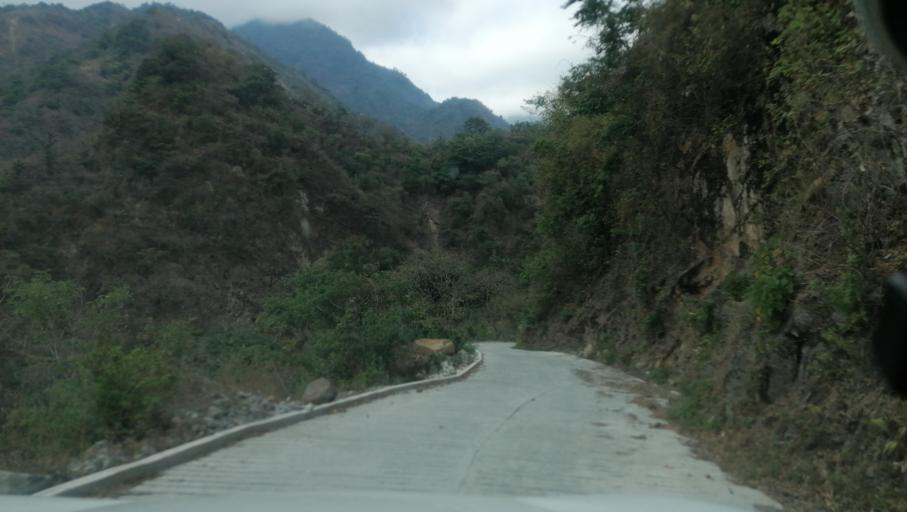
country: MX
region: Chiapas
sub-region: Cacahoatan
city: Benito Juarez
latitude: 15.1646
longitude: -92.1794
